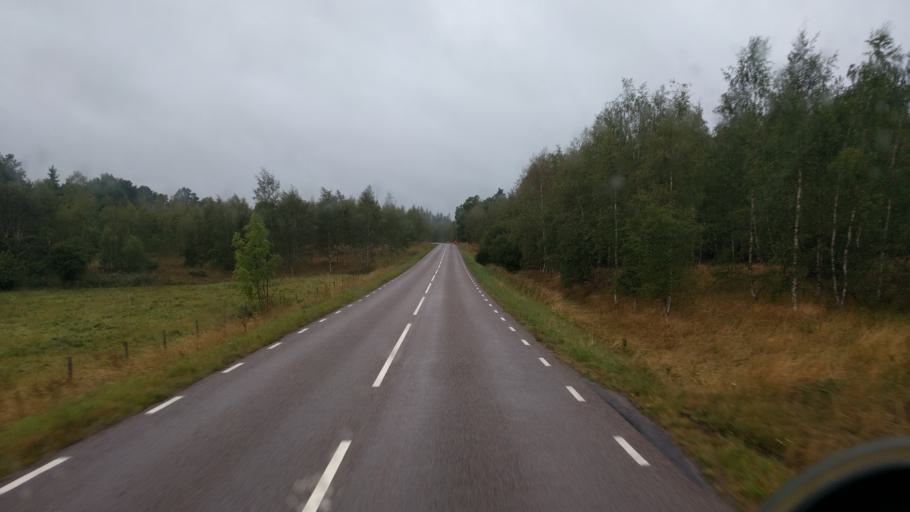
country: SE
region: Kalmar
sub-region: Vasterviks Kommun
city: Ankarsrum
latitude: 57.7949
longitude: 16.3699
